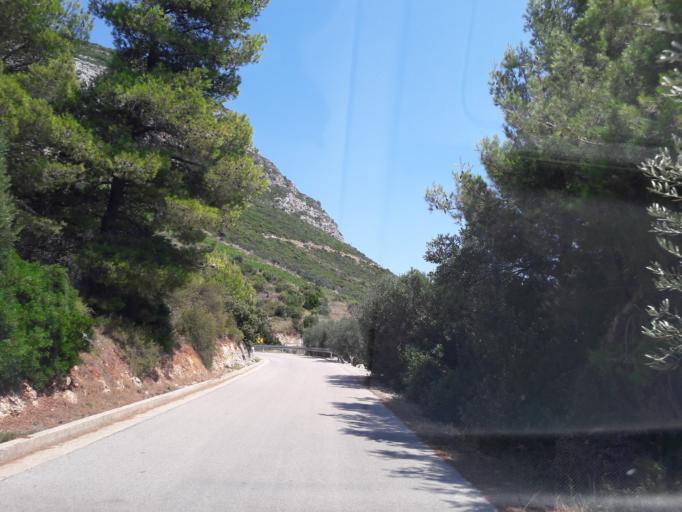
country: HR
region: Dubrovacko-Neretvanska
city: Blato
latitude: 42.9031
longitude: 17.4298
